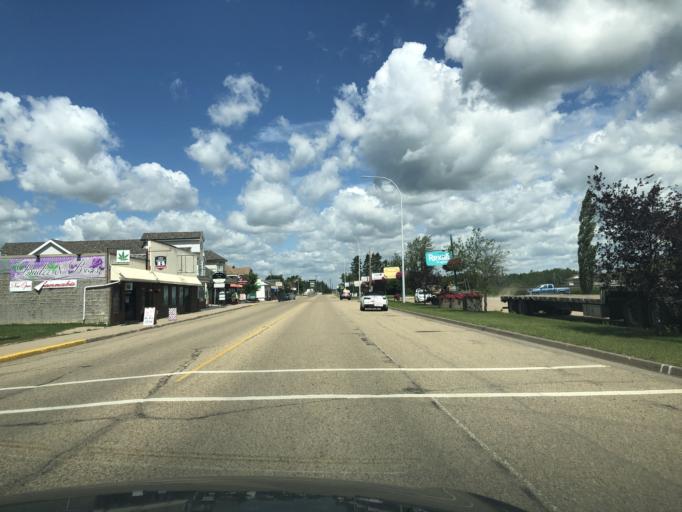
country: CA
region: Alberta
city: Millet
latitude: 53.0946
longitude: -113.4715
